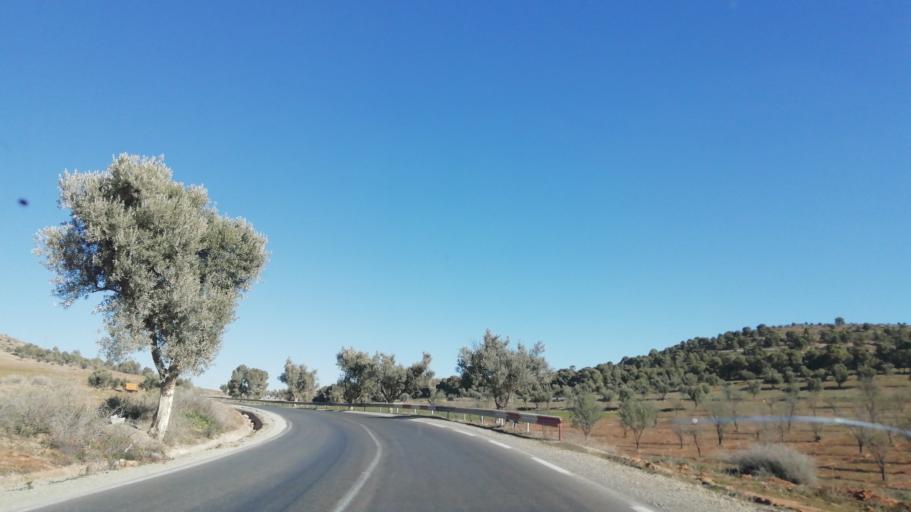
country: DZ
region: Mascara
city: Mascara
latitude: 35.2416
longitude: 0.1188
